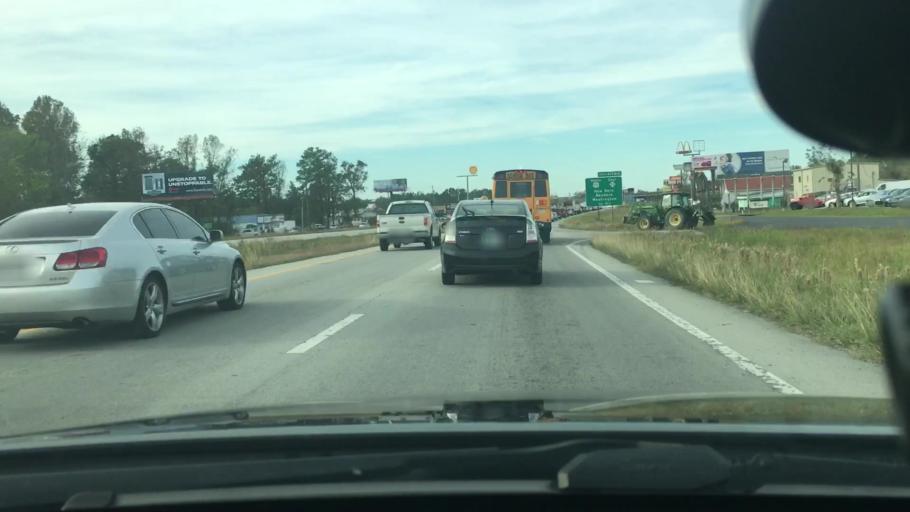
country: US
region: North Carolina
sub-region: Craven County
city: James City
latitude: 35.0783
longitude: -77.0297
